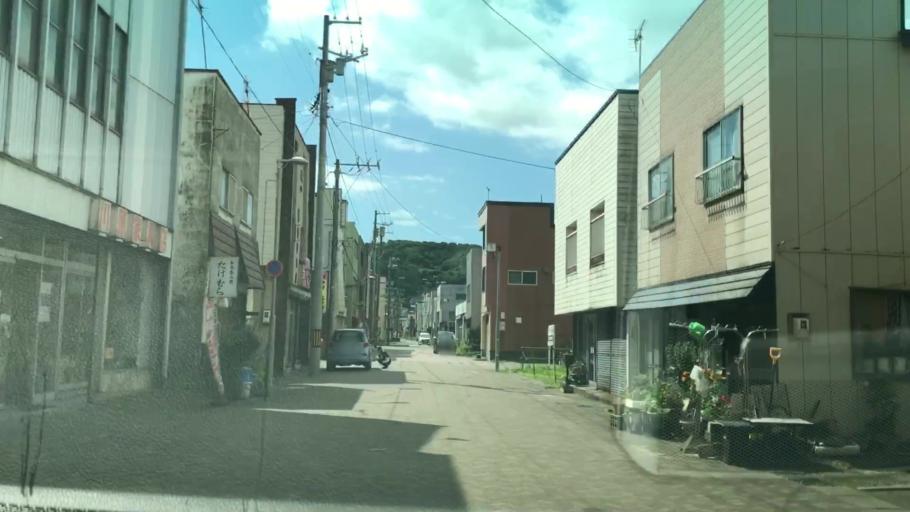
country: JP
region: Hokkaido
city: Muroran
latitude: 42.3353
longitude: 141.0121
